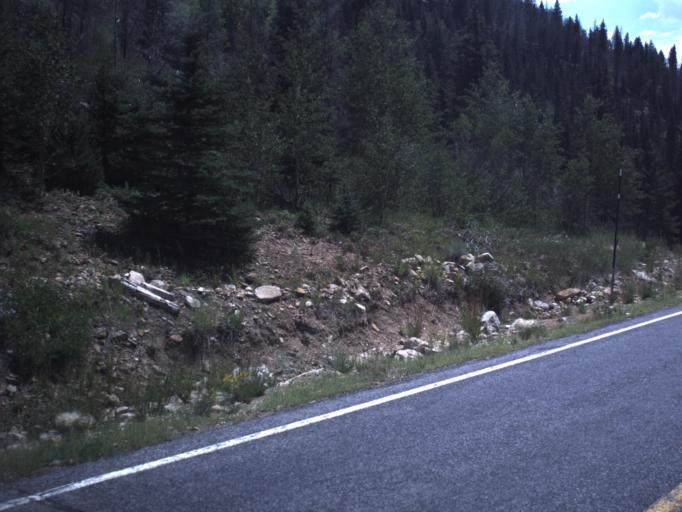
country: US
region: Utah
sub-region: Emery County
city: Huntington
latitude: 39.5155
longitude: -111.1554
